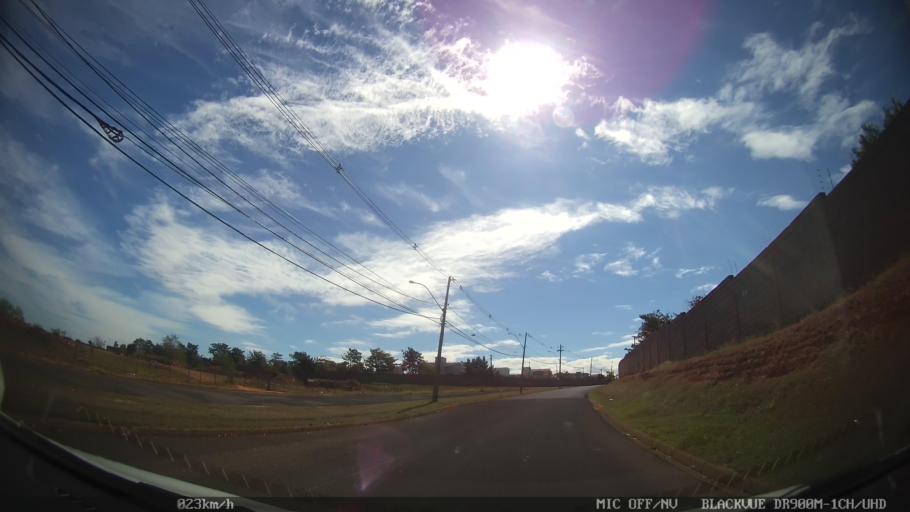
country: BR
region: Sao Paulo
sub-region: Bady Bassitt
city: Bady Bassitt
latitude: -20.8262
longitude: -49.4829
